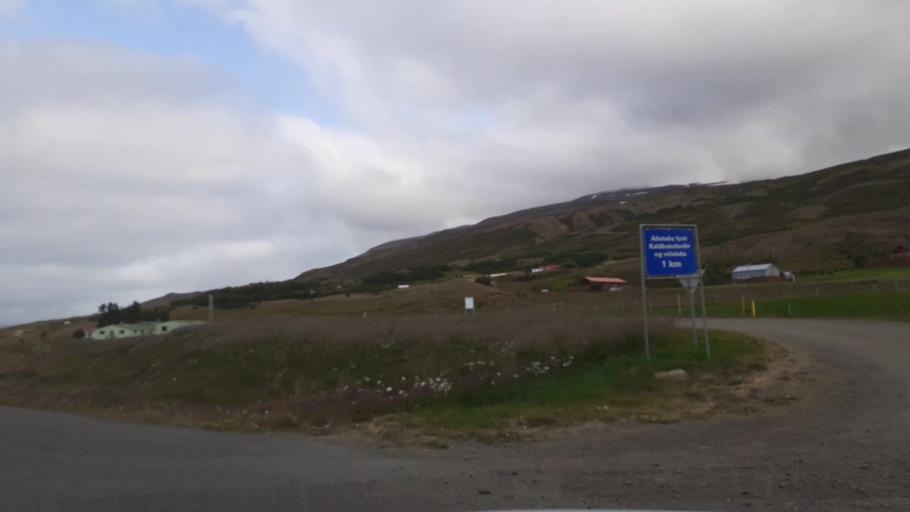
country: IS
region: Northeast
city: Akureyri
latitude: 65.9523
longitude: -18.1779
